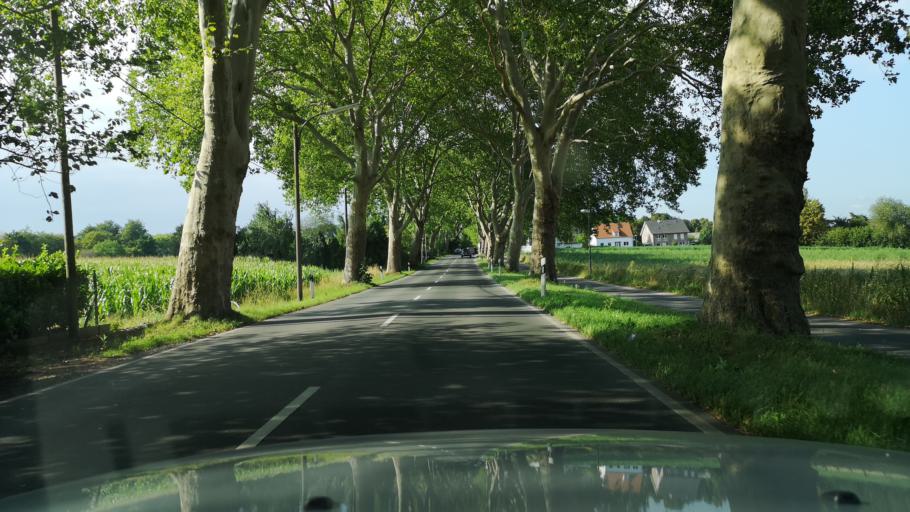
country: DE
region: North Rhine-Westphalia
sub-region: Regierungsbezirk Arnsberg
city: Dortmund
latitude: 51.4714
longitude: 7.5111
